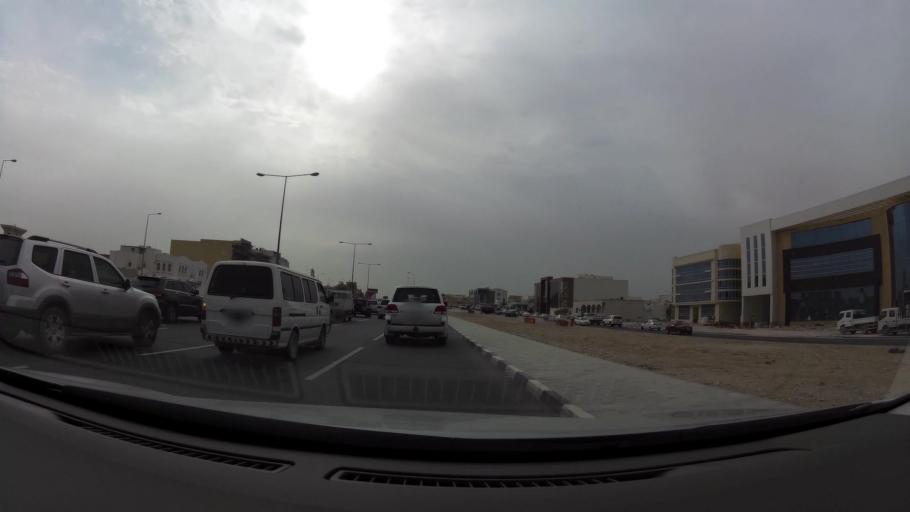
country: QA
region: Baladiyat ar Rayyan
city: Ar Rayyan
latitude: 25.3353
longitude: 51.4781
